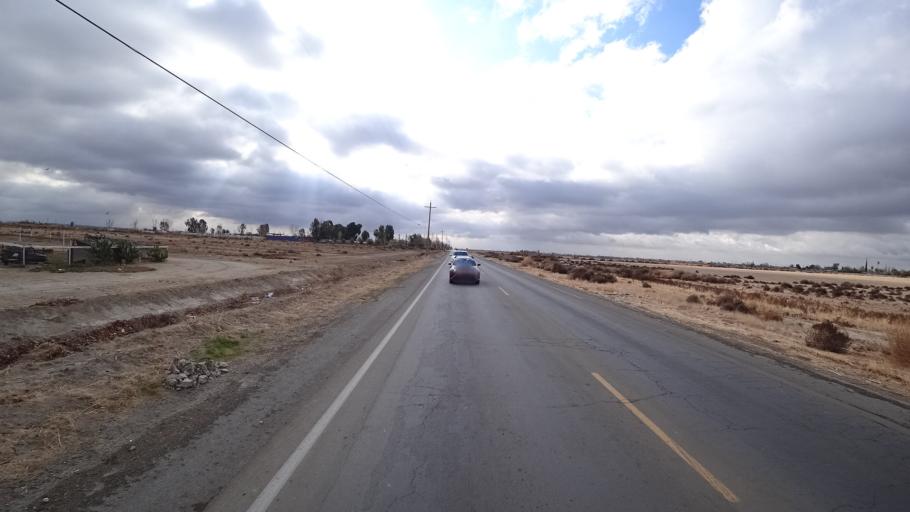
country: US
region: California
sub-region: Kern County
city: Greenfield
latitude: 35.3048
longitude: -118.9854
